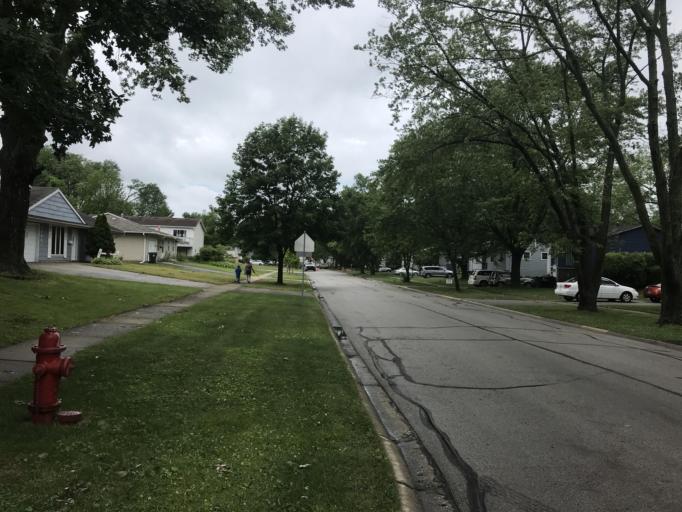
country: US
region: Illinois
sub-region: DuPage County
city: Woodridge
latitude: 41.7453
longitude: -88.0446
